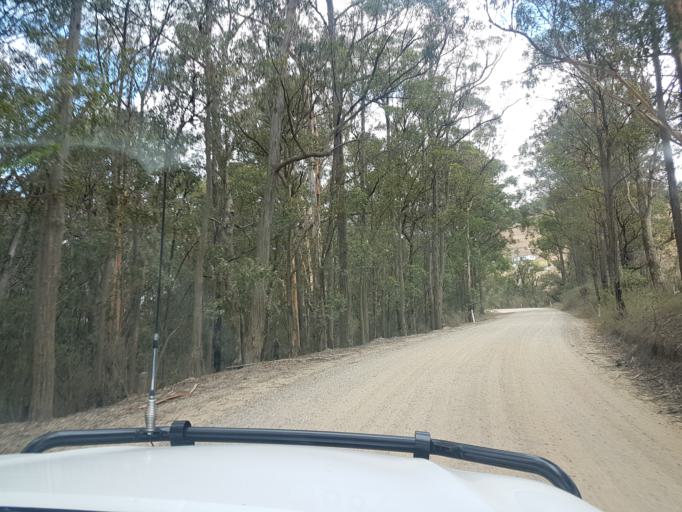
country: AU
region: Victoria
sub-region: East Gippsland
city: Bairnsdale
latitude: -37.6881
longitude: 147.5617
